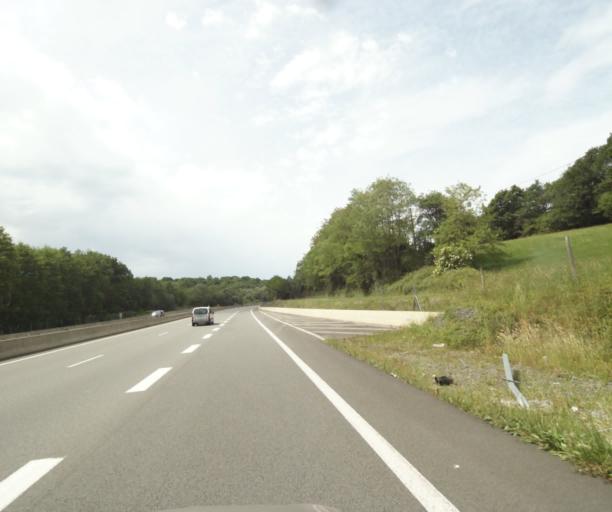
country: FR
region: Aquitaine
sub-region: Departement des Pyrenees-Atlantiques
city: Mouguerre
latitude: 43.4638
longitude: -1.4253
